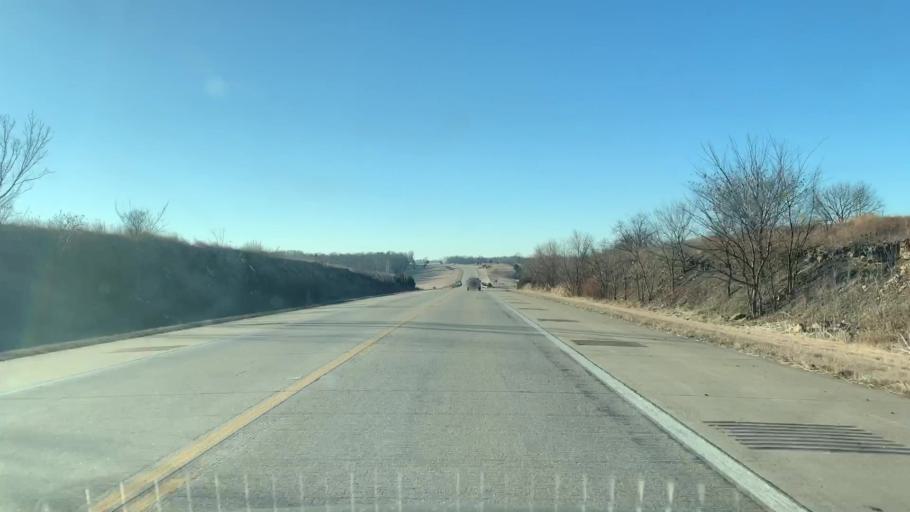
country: US
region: Kansas
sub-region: Crawford County
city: Arma
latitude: 37.5882
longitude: -94.7055
